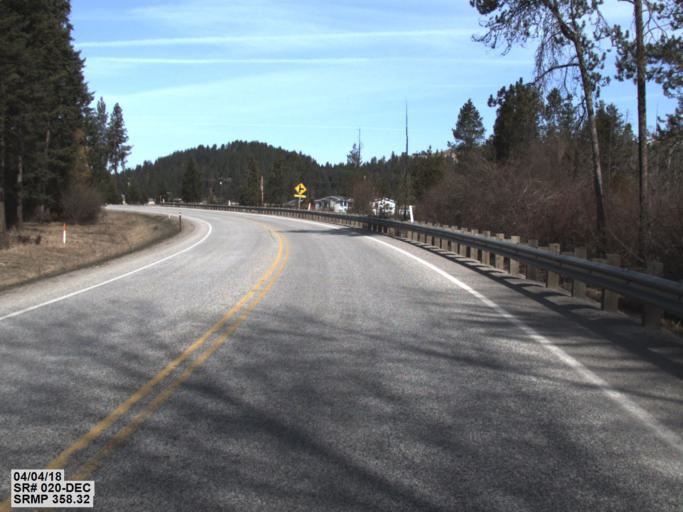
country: US
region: Washington
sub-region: Stevens County
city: Colville
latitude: 48.5380
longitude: -117.8243
